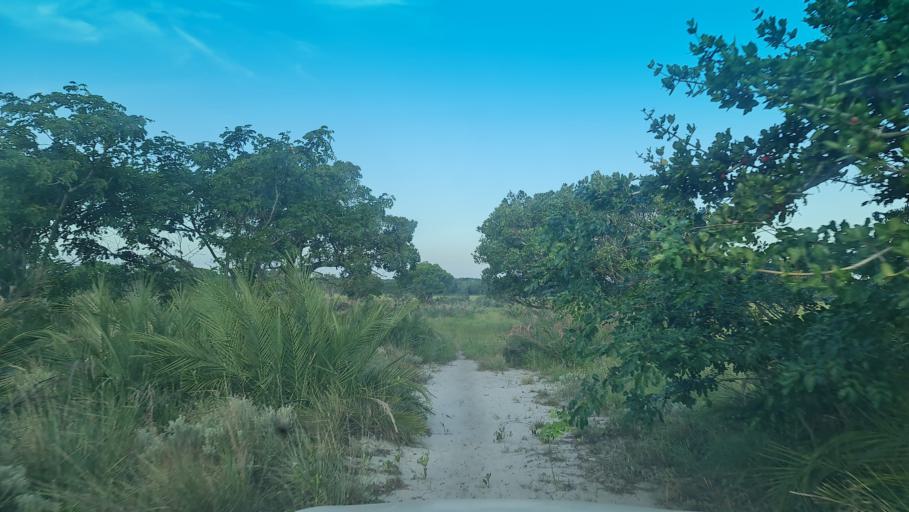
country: MZ
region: Gaza
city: Macia
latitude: -25.2133
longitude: 33.0550
